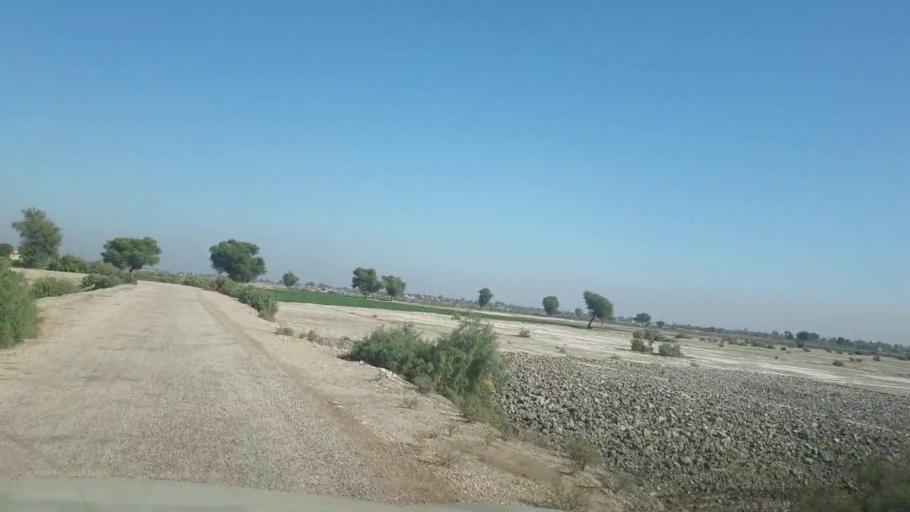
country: PK
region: Sindh
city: Bhan
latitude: 26.5383
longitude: 67.6460
